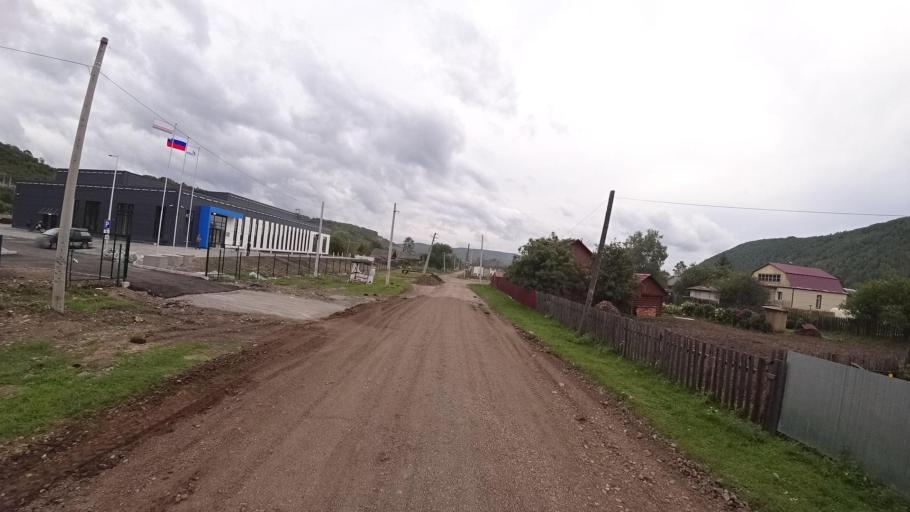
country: RU
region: Jewish Autonomous Oblast
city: Khingansk
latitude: 49.0036
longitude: 131.0524
